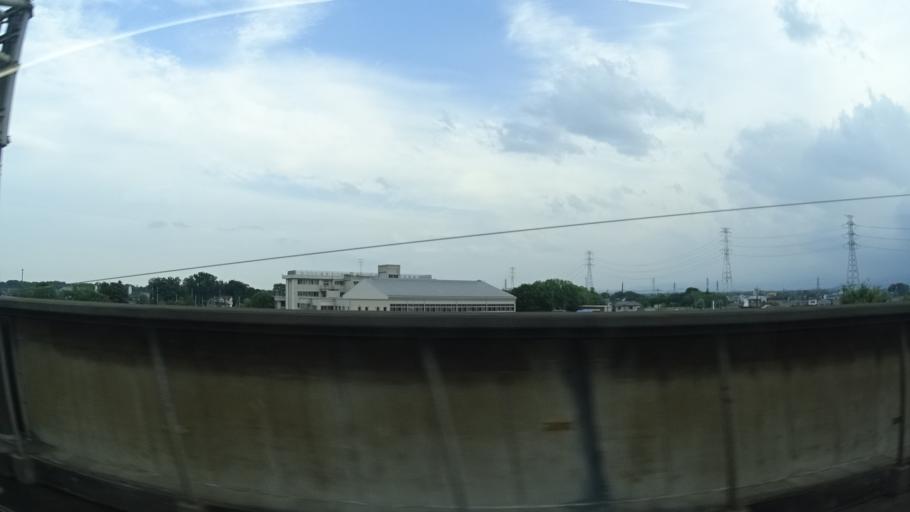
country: JP
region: Saitama
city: Kumagaya
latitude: 36.1528
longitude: 139.3395
